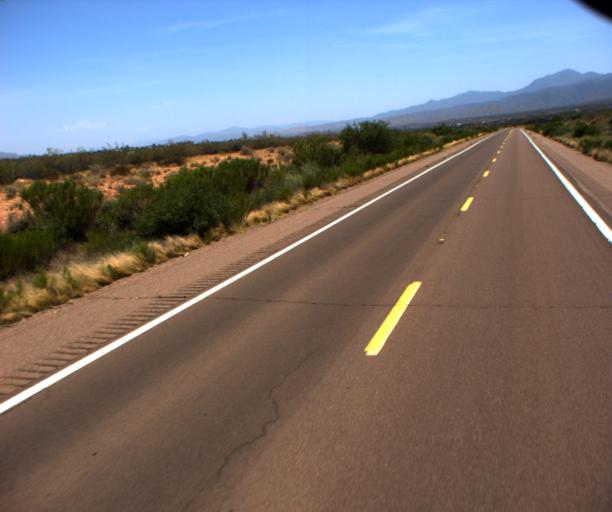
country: US
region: Arizona
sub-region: Gila County
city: Tonto Basin
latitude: 33.8875
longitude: -111.3119
